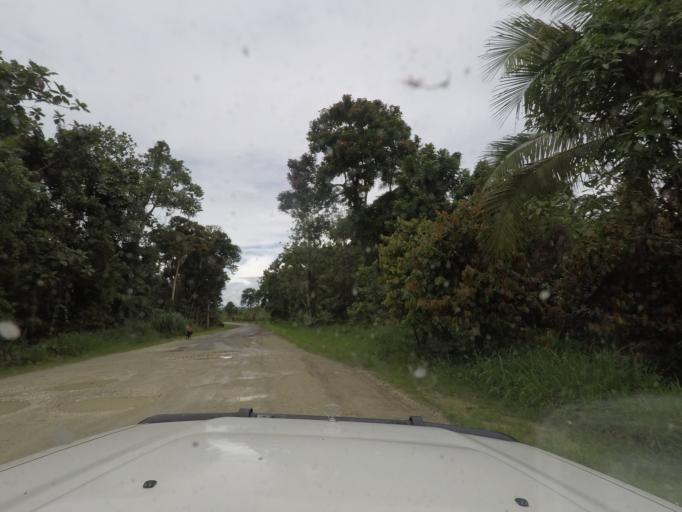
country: PG
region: Eastern Highlands
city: Goroka
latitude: -5.6707
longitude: 145.4994
